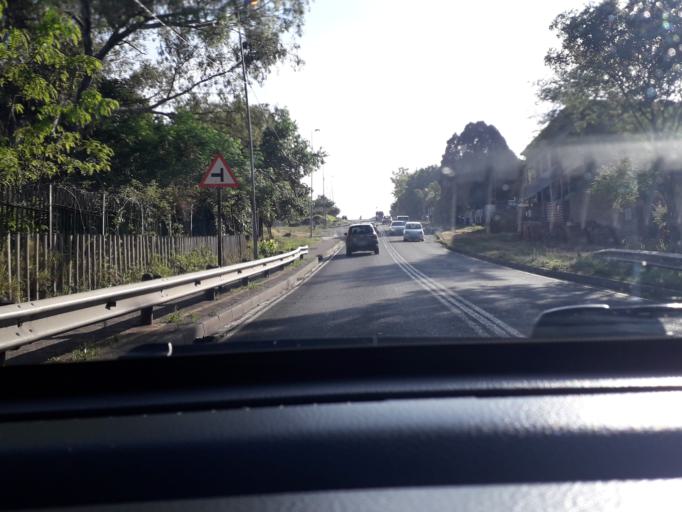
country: ZA
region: Gauteng
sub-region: City of Johannesburg Metropolitan Municipality
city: Modderfontein
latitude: -26.0697
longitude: 28.0698
